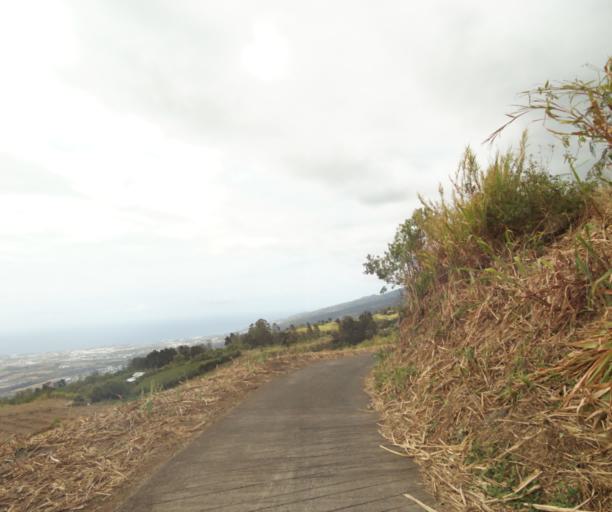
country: RE
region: Reunion
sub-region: Reunion
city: Saint-Paul
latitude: -21.0195
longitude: 55.3254
